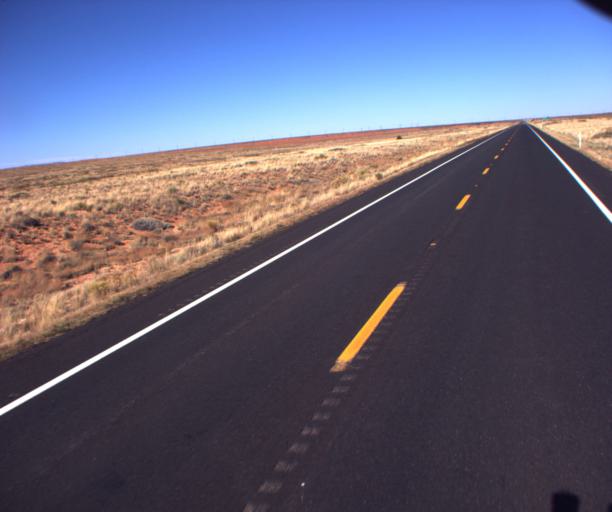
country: US
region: Arizona
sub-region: Coconino County
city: Kaibito
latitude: 36.3798
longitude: -110.8886
